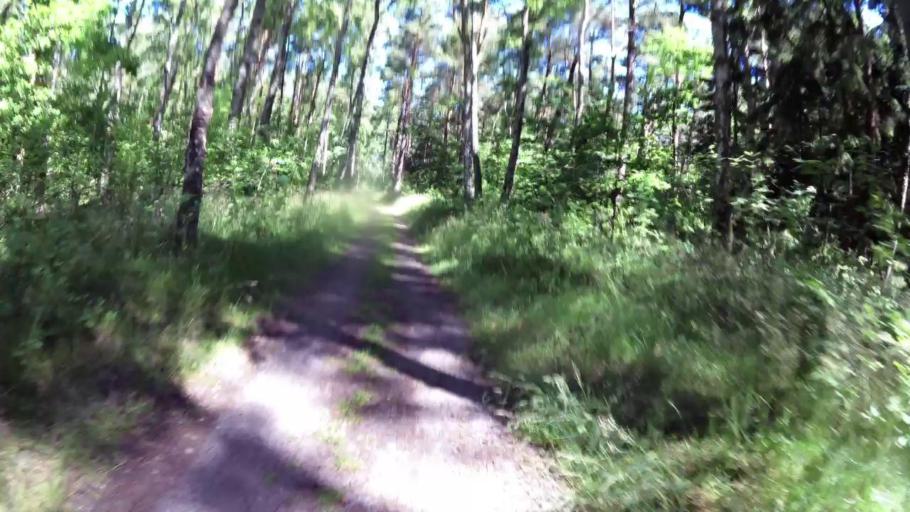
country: PL
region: West Pomeranian Voivodeship
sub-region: Powiat kamienski
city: Dziwnow
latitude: 54.0438
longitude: 14.8500
